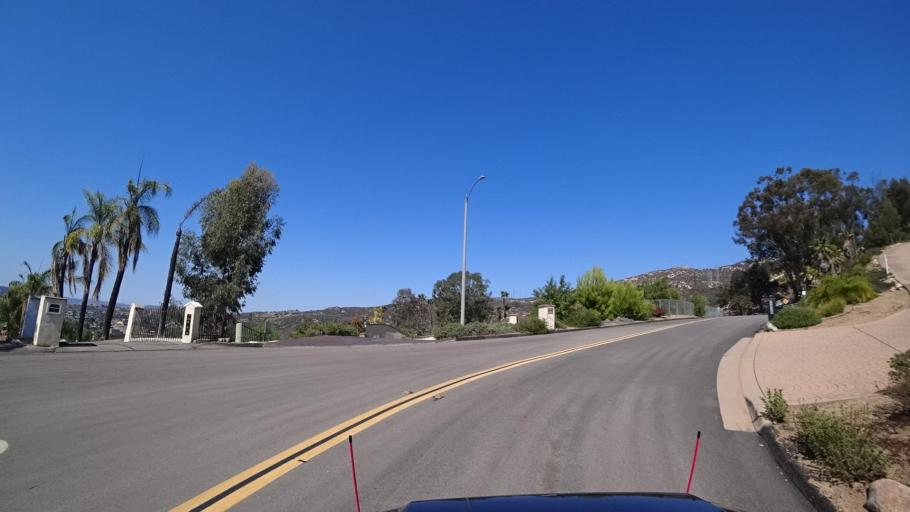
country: US
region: California
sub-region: San Diego County
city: Granite Hills
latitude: 32.8049
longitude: -116.8955
